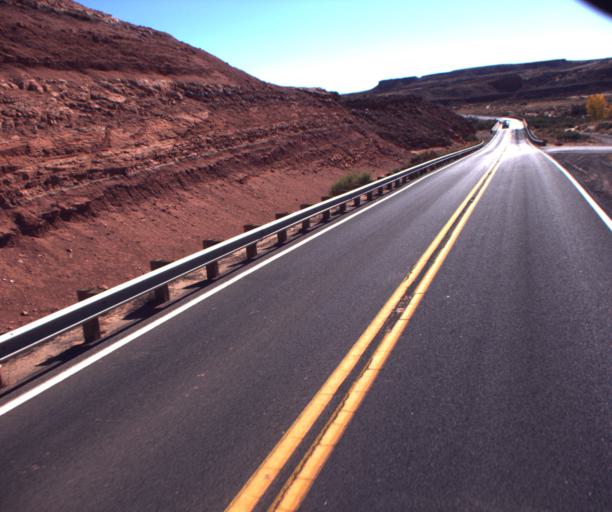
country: US
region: Arizona
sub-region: Coconino County
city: Tuba City
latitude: 36.1050
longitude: -111.2032
